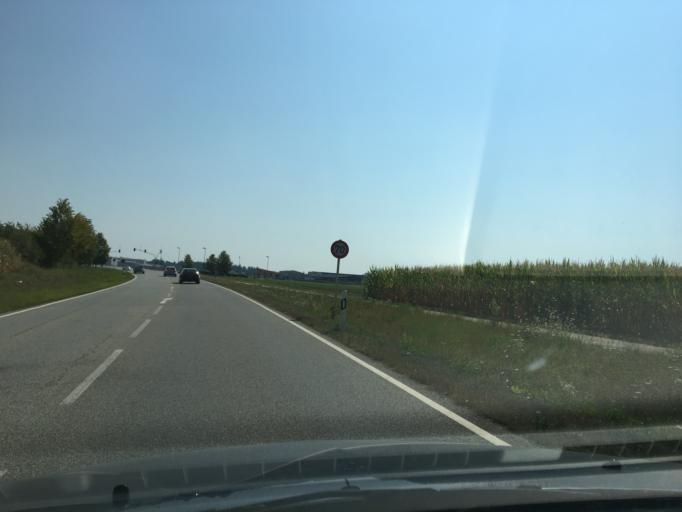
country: DE
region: Bavaria
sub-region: Upper Bavaria
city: Muehldorf
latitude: 48.2517
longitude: 12.5346
